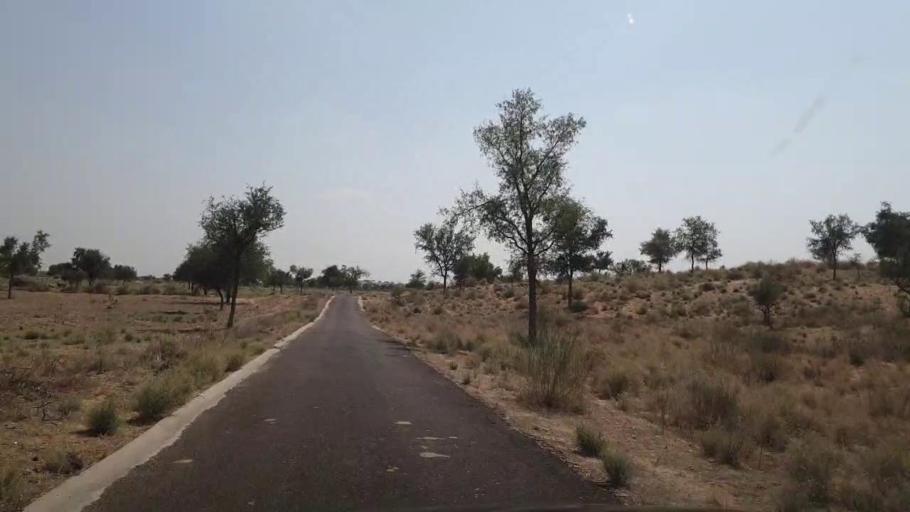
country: PK
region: Sindh
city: Islamkot
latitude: 25.0927
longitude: 70.7318
